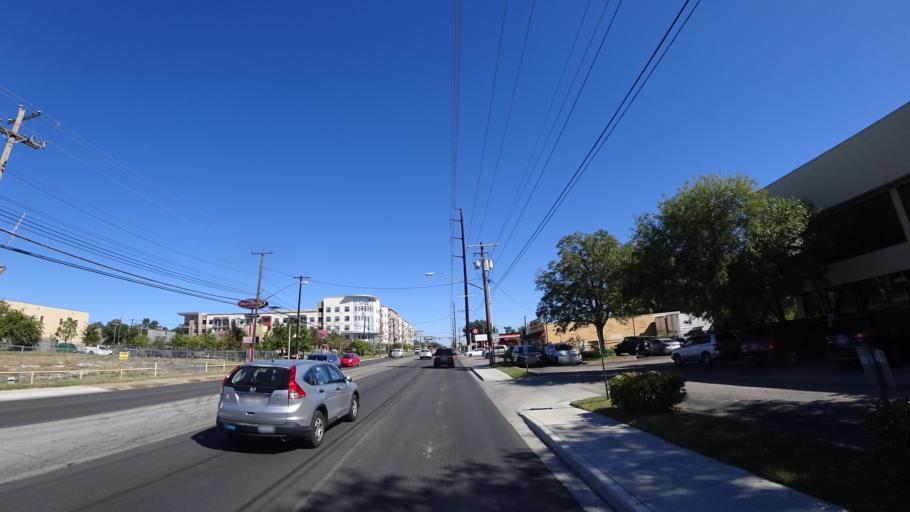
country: US
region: Texas
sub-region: Travis County
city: Austin
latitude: 30.3201
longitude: -97.7299
